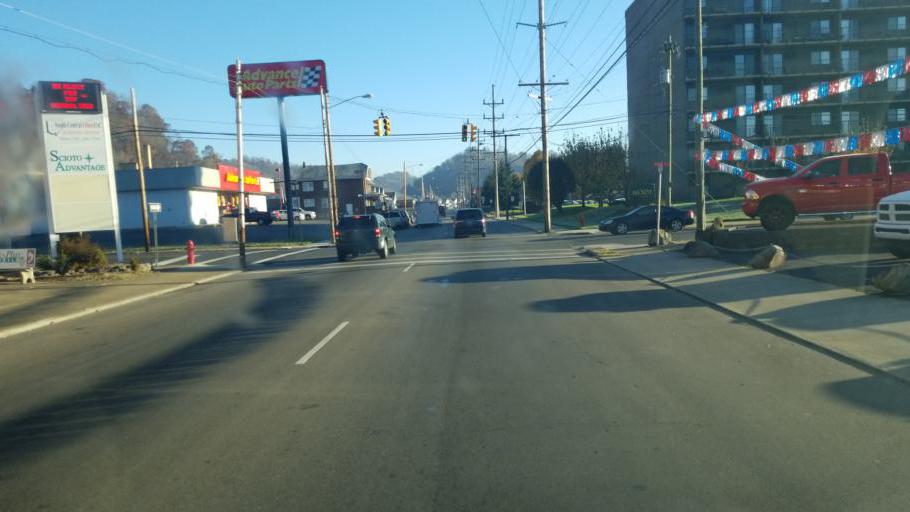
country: US
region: Ohio
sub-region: Scioto County
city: New Boston
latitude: 38.7510
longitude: -82.9377
